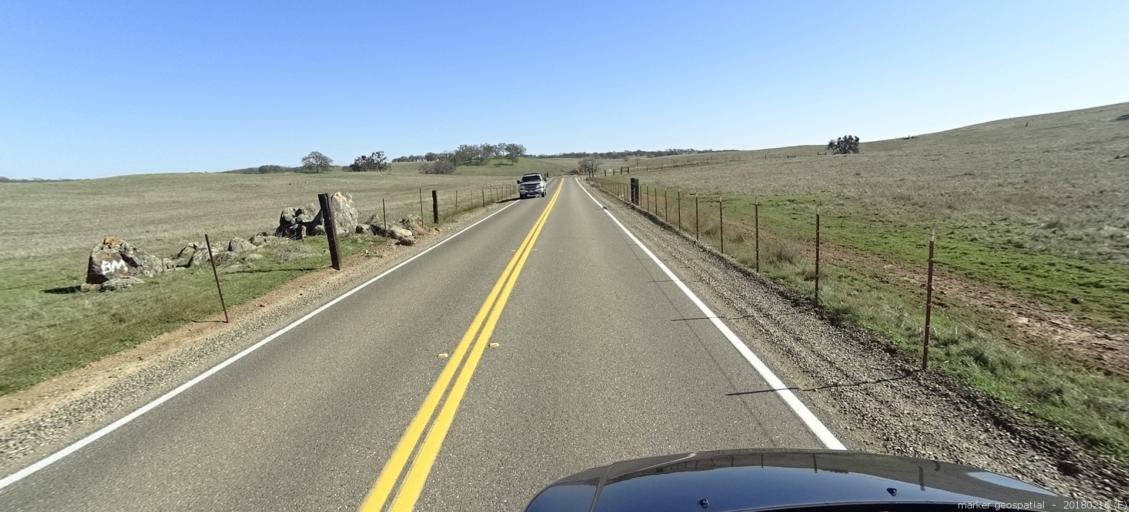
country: US
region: California
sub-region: Sacramento County
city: Rancho Murieta
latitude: 38.5578
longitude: -121.1197
